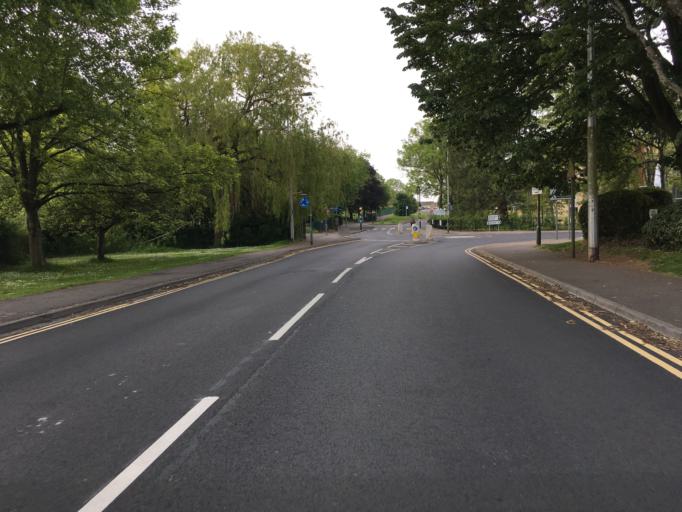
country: GB
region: England
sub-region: North Somerset
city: Nailsea
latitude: 51.4322
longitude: -2.7579
